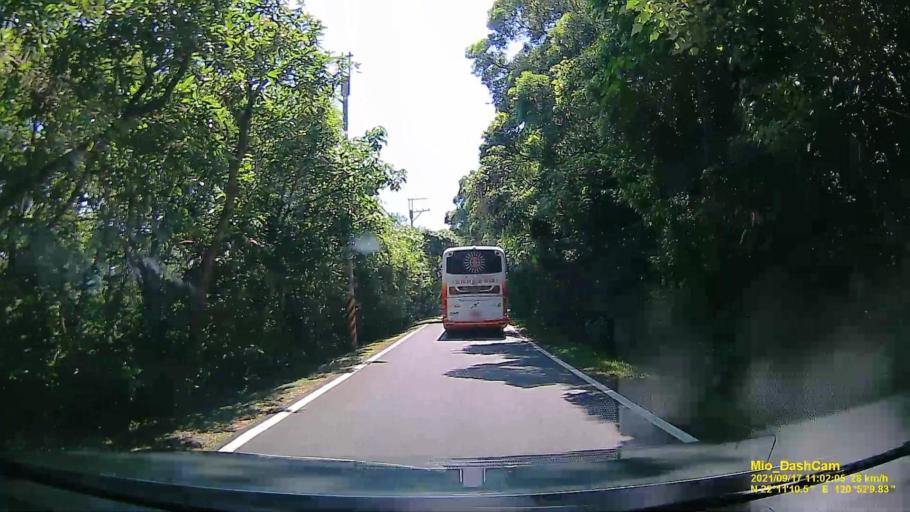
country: TW
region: Taiwan
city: Hengchun
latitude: 22.1862
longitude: 120.8695
